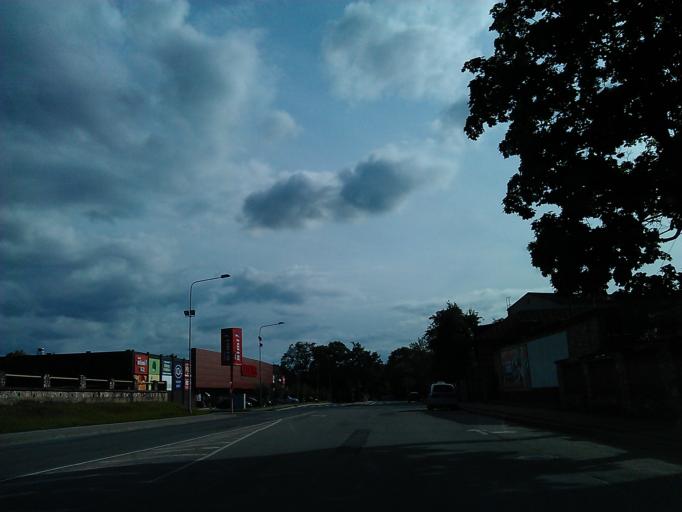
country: LV
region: Cesu Rajons
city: Cesis
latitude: 57.3108
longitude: 25.2781
